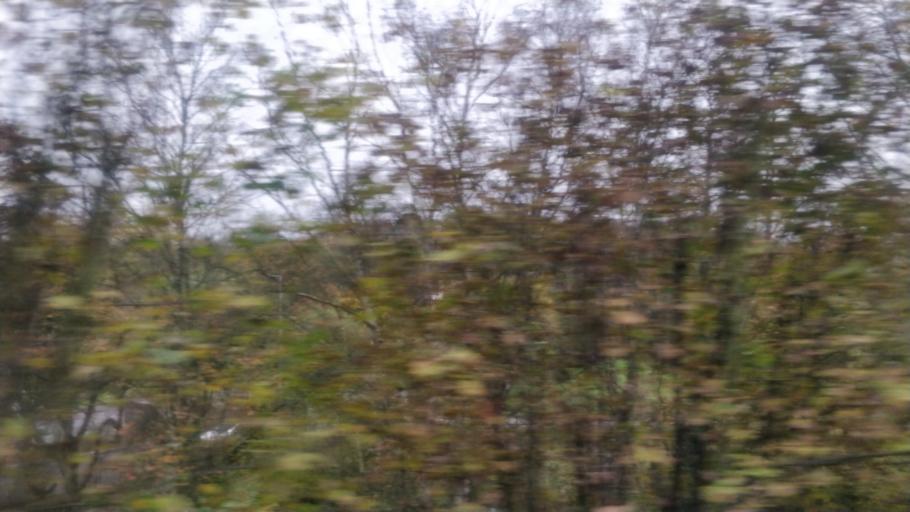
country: GB
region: England
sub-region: Borough of Wigan
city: Shevington
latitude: 53.5599
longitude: -2.6959
